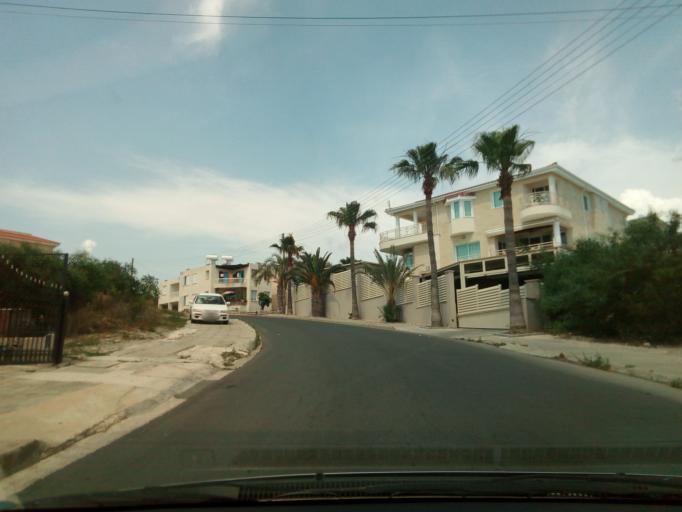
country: CY
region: Pafos
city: Chlorakas
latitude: 34.7895
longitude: 32.4138
